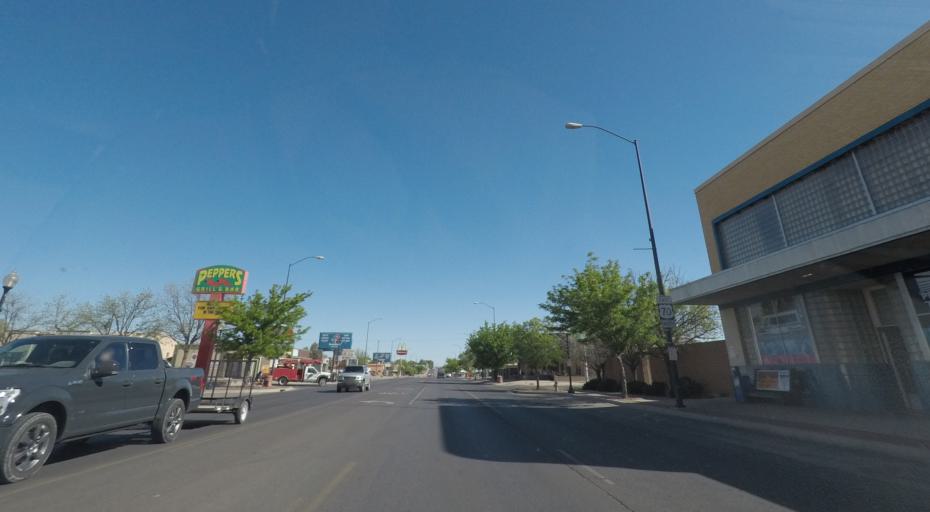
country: US
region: New Mexico
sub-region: Chaves County
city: Roswell
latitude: 33.3982
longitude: -104.5228
